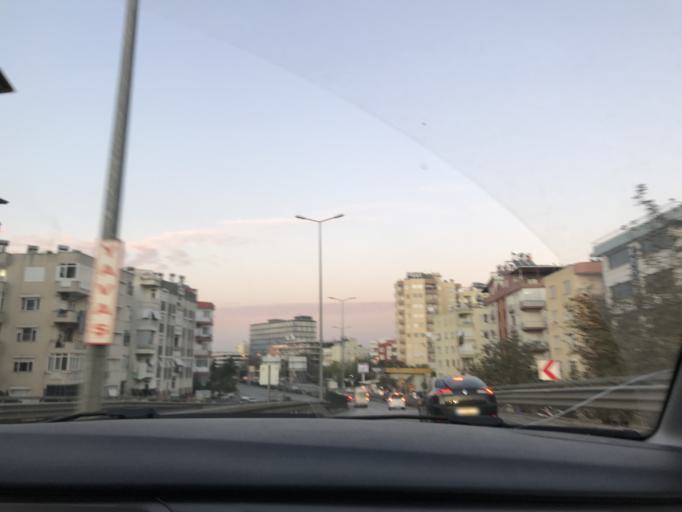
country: TR
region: Antalya
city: Antalya
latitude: 36.8973
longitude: 30.7140
